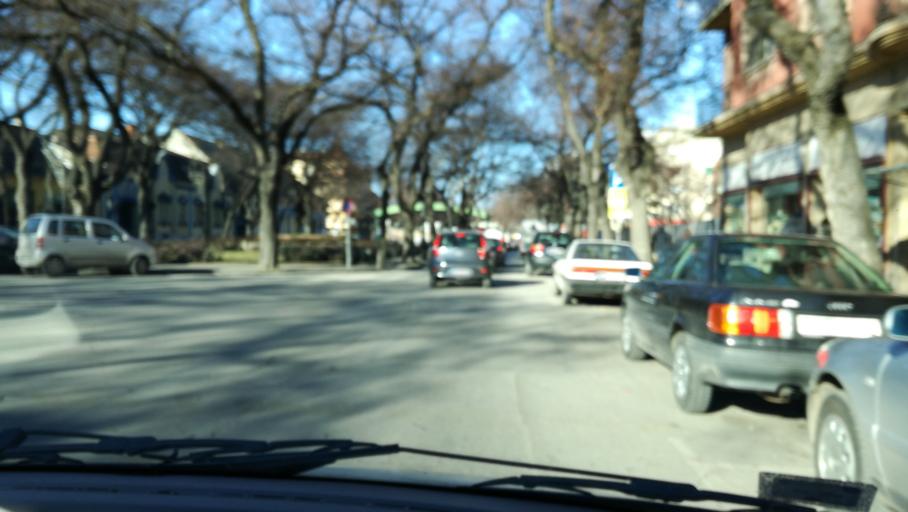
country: RS
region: Autonomna Pokrajina Vojvodina
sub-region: Severnobacki Okrug
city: Subotica
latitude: 46.1008
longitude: 19.6613
